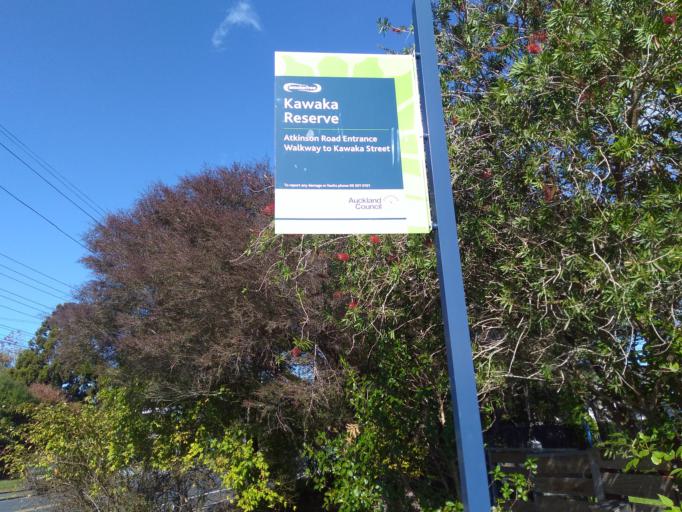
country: NZ
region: Auckland
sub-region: Auckland
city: Titirangi
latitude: -36.9283
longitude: 174.6546
